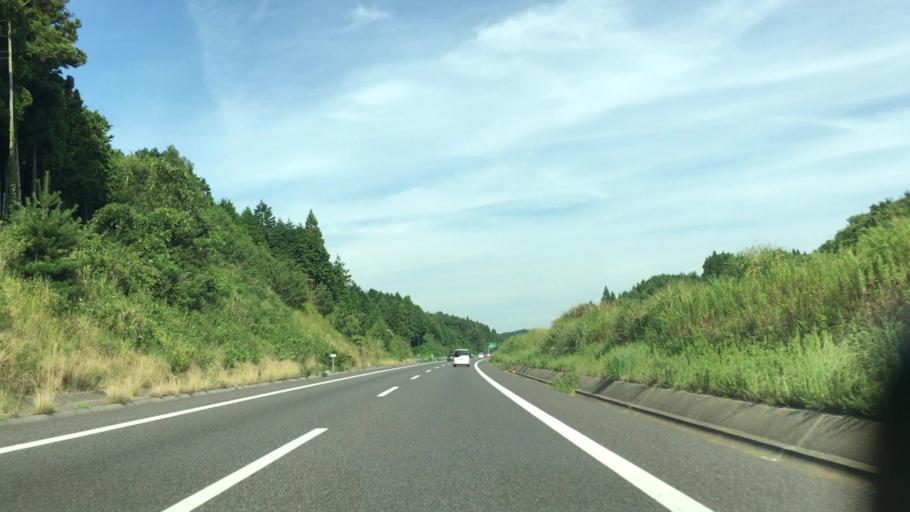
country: JP
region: Shiga Prefecture
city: Hino
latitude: 34.9276
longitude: 136.2415
